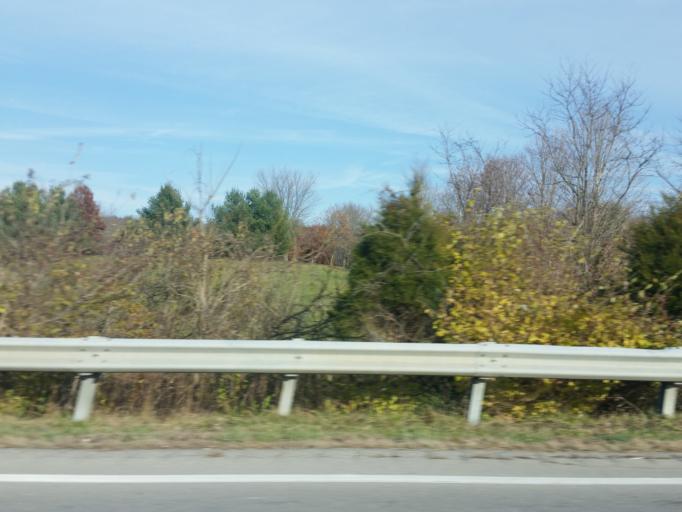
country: US
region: Kentucky
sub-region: Campbell County
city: Claryville
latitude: 38.8416
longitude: -84.3732
